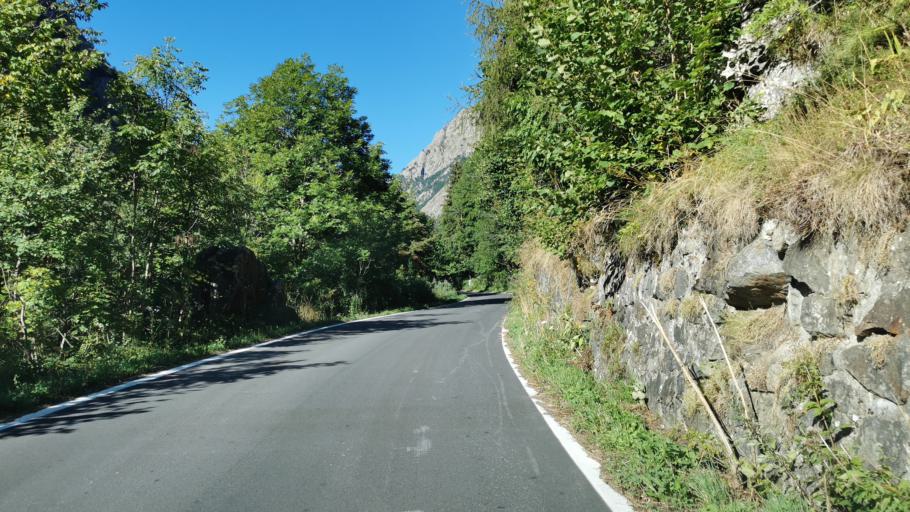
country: IT
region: Piedmont
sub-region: Provincia di Cuneo
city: Demonte
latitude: 44.2255
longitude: 7.2984
